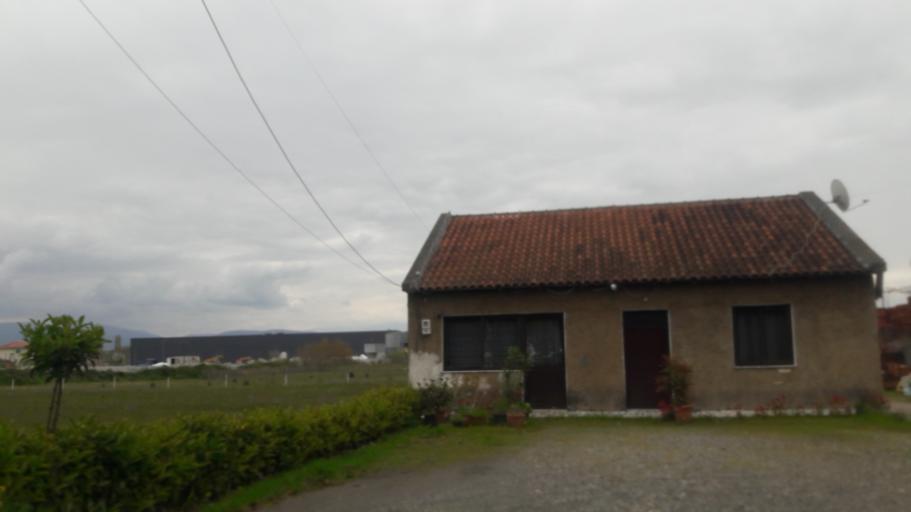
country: AL
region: Shkoder
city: Vukatane
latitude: 41.9697
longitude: 19.5395
